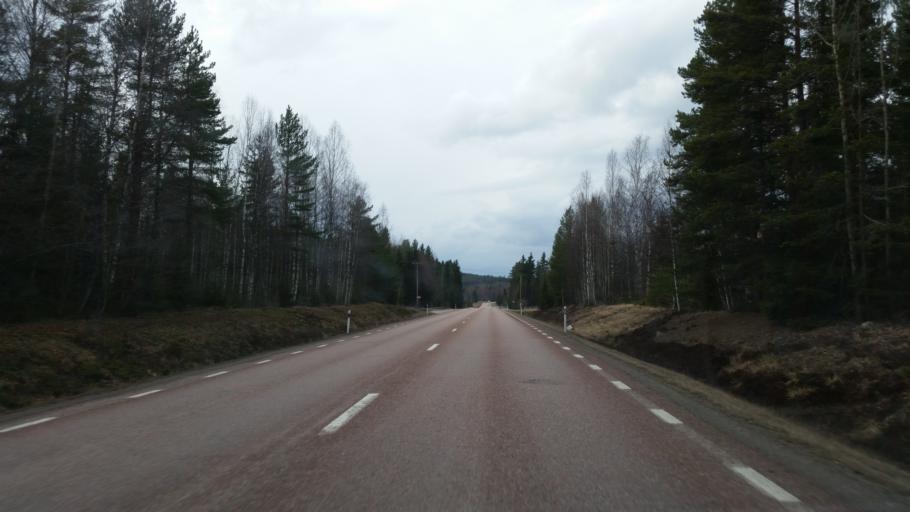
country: SE
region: Gaevleborg
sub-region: Ljusdals Kommun
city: Jaervsoe
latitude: 61.7807
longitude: 16.1414
